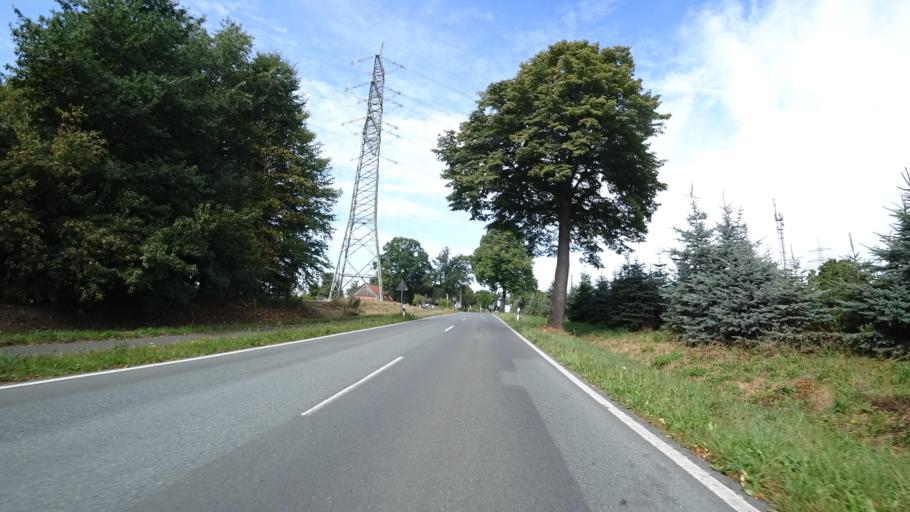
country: DE
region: North Rhine-Westphalia
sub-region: Regierungsbezirk Detmold
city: Steinhagen
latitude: 51.9560
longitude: 8.3960
